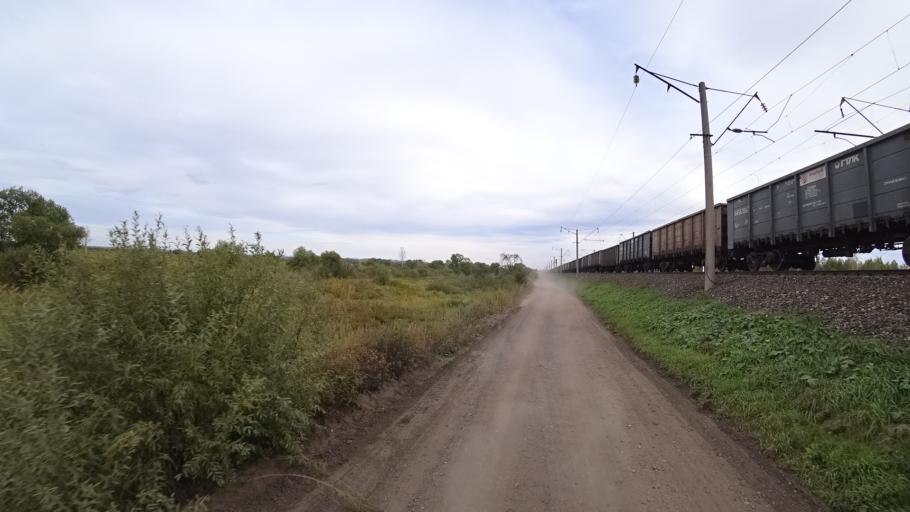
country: RU
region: Amur
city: Arkhara
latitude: 49.3589
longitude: 130.1514
